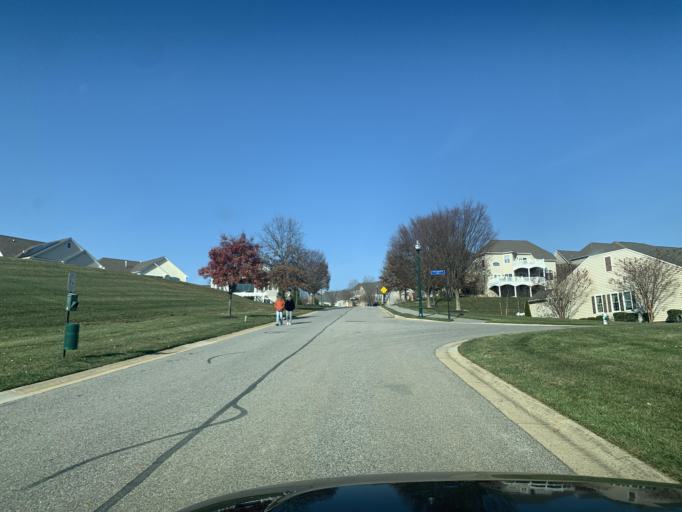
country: US
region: Maryland
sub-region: Harford County
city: Havre de Grace
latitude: 39.5517
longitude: -76.1249
